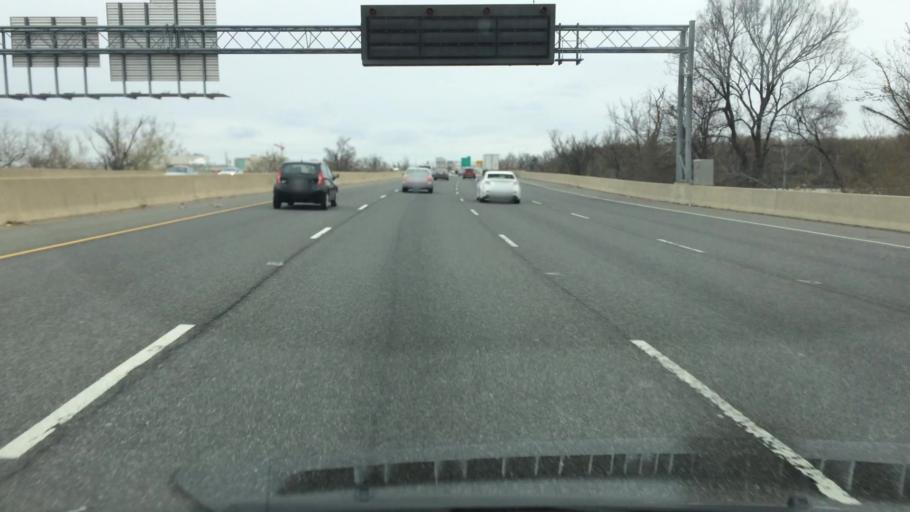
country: US
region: Virginia
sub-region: City of Alexandria
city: Alexandria
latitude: 38.8053
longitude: -77.0224
